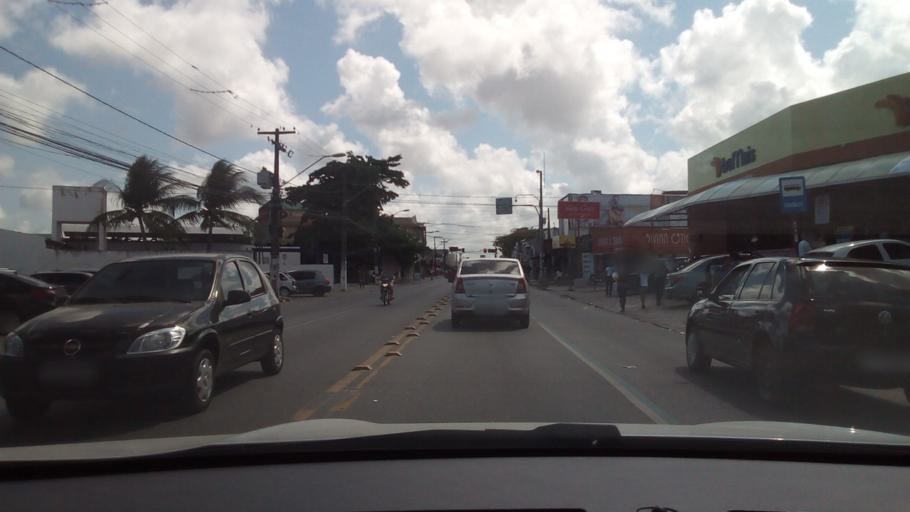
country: BR
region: Paraiba
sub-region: Joao Pessoa
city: Joao Pessoa
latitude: -7.1707
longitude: -34.8390
